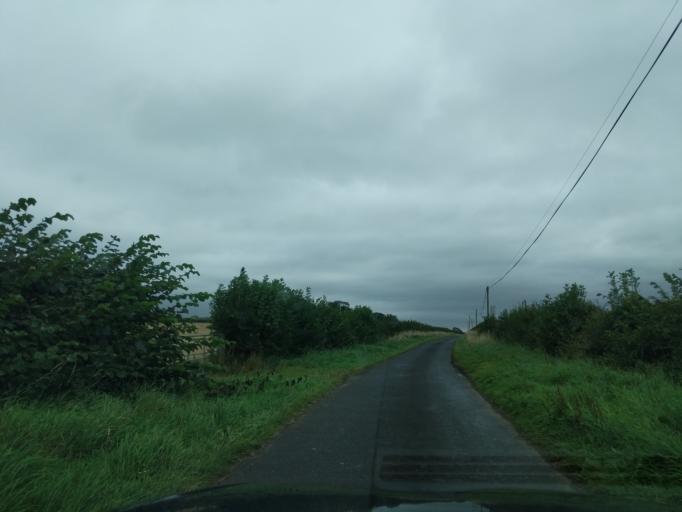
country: GB
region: Scotland
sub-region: The Scottish Borders
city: Kelso
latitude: 55.5934
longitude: -2.5213
